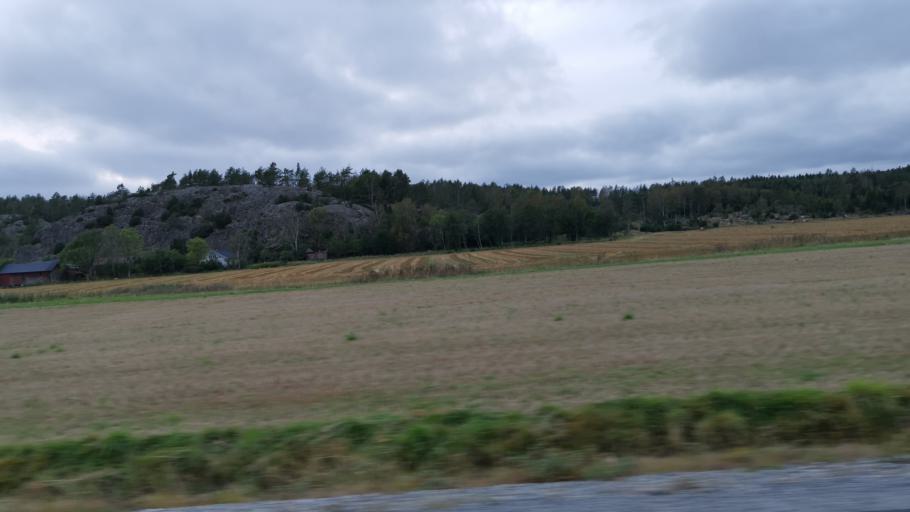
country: SE
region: Vaestra Goetaland
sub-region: Tanums Kommun
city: Tanumshede
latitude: 58.6490
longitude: 11.3396
